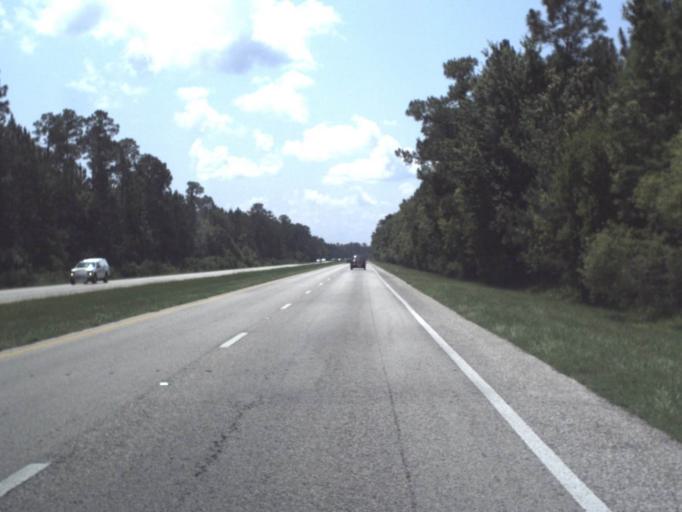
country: US
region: Florida
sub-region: Saint Johns County
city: Saint Augustine Shores
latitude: 29.7477
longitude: -81.3112
